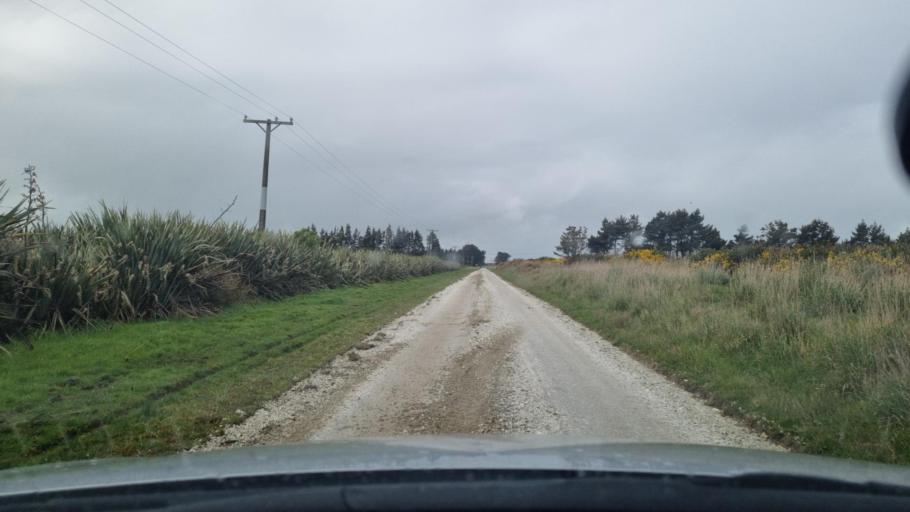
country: NZ
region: Southland
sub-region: Invercargill City
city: Invercargill
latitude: -46.4948
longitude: 168.4222
